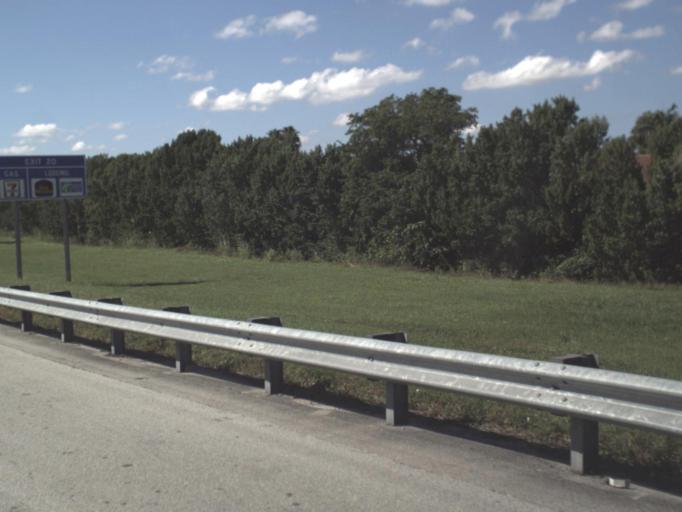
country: US
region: Florida
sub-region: Miami-Dade County
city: Kendale Lakes
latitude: 25.6986
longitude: -80.3846
